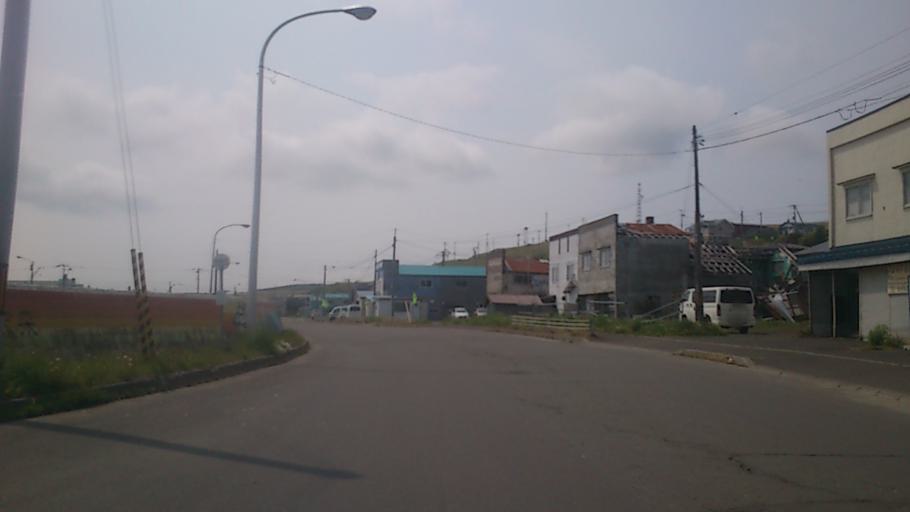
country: JP
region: Hokkaido
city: Nemuro
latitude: 43.2869
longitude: 145.5827
